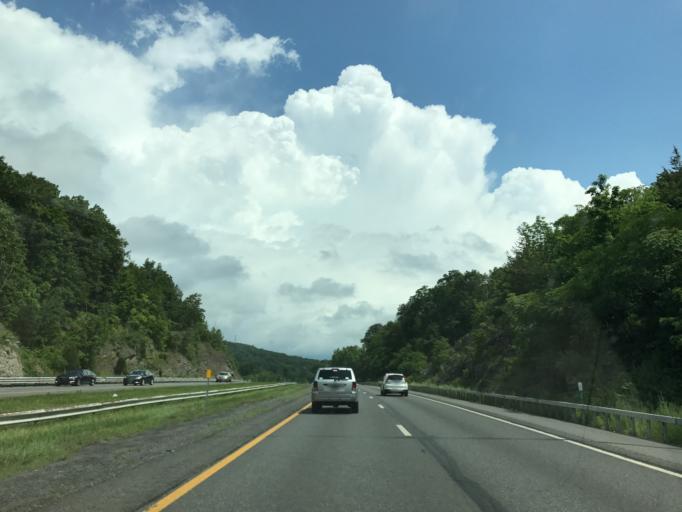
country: US
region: New York
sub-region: Greene County
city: Coxsackie
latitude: 42.3572
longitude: -73.8490
